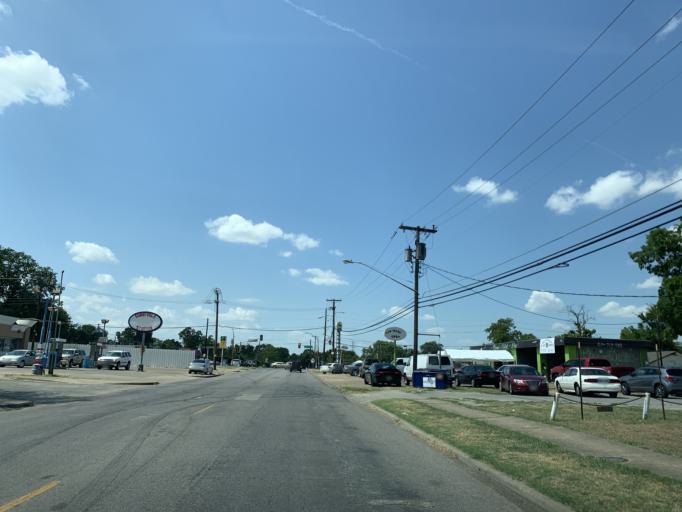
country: US
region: Texas
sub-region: Dallas County
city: Dallas
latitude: 32.7107
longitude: -96.7834
